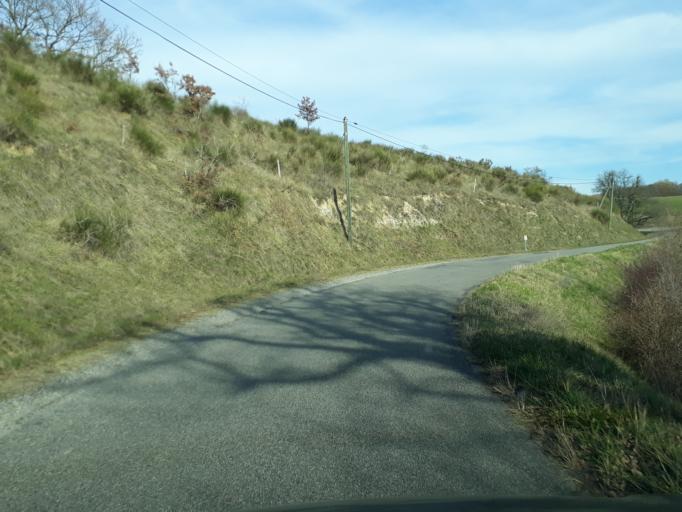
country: FR
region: Midi-Pyrenees
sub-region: Departement de la Haute-Garonne
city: Montesquieu-Volvestre
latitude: 43.1824
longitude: 1.2968
